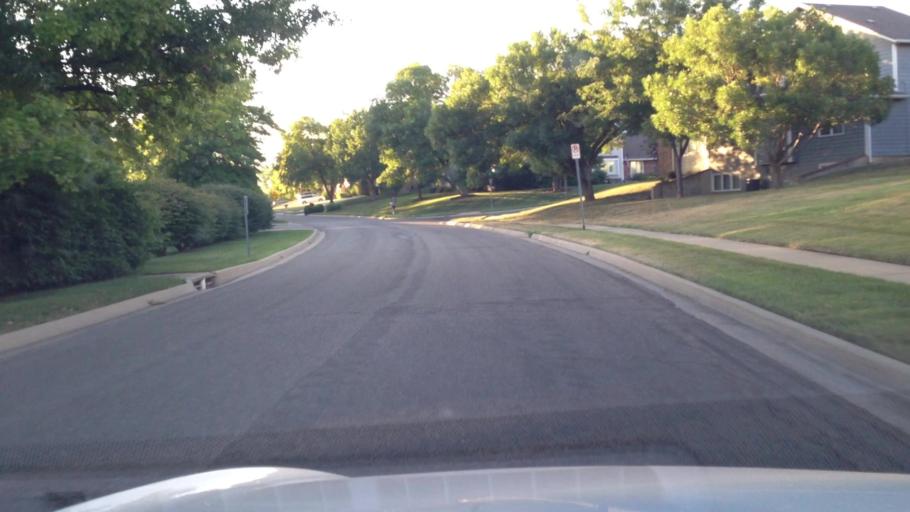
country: US
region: Kansas
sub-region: Douglas County
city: Lawrence
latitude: 38.9435
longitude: -95.2885
